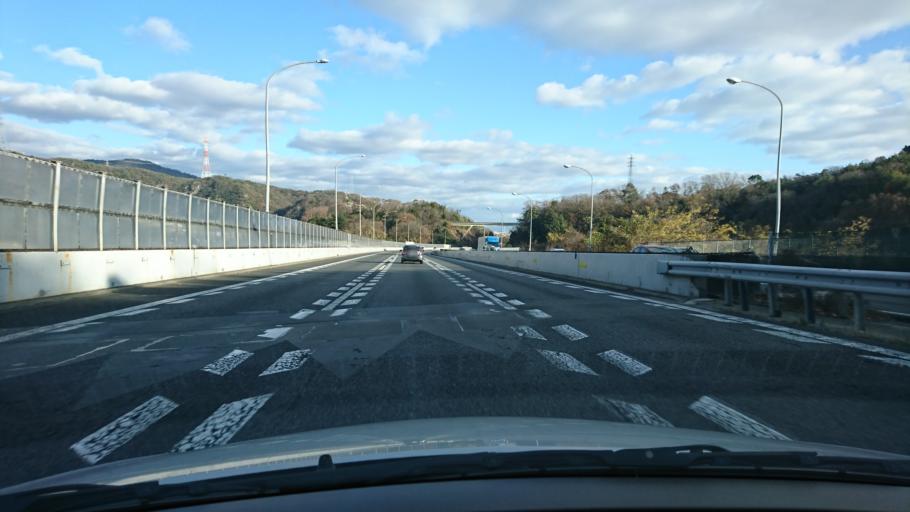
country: JP
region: Hyogo
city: Takarazuka
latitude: 34.8248
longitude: 135.3099
